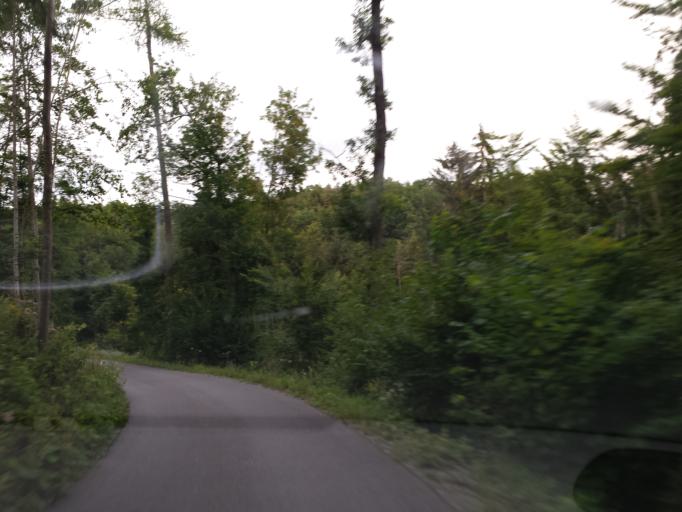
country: AT
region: Styria
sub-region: Politischer Bezirk Graz-Umgebung
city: Stattegg
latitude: 47.1397
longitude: 15.4420
